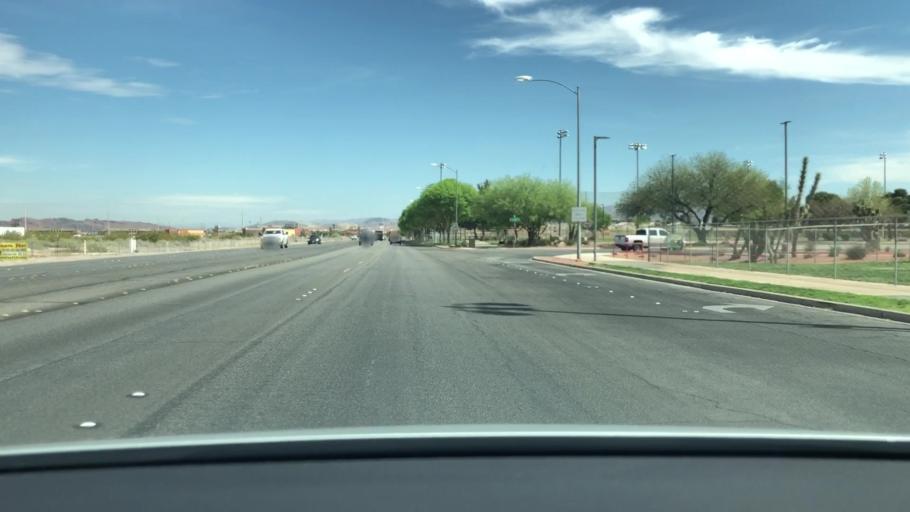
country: US
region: Nevada
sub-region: Clark County
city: Whitney
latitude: 36.0838
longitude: -115.0426
